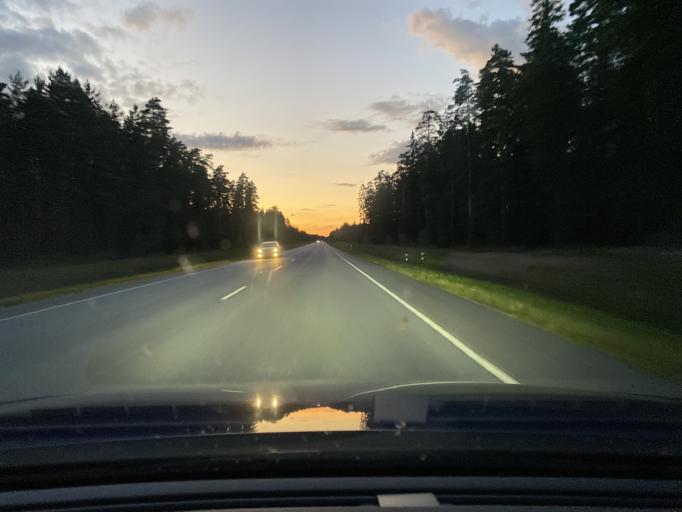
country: FI
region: Varsinais-Suomi
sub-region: Loimaa
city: Oripaeae
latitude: 60.9146
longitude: 22.6912
